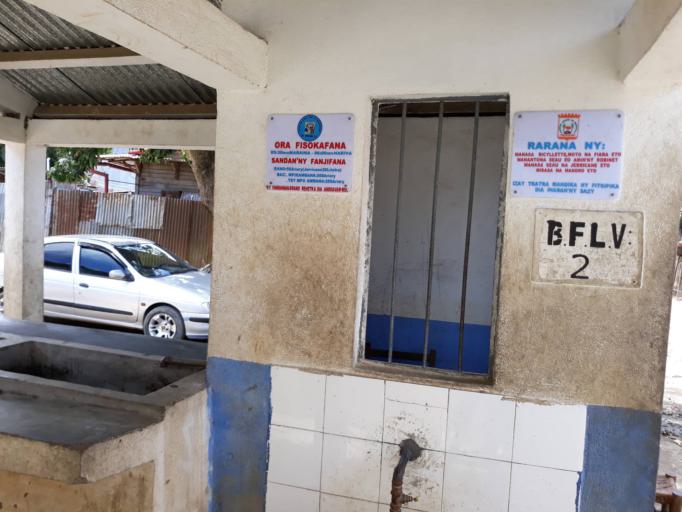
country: MG
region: Atsinanana
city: Ampasimanolotra
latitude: -18.8219
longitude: 49.0731
